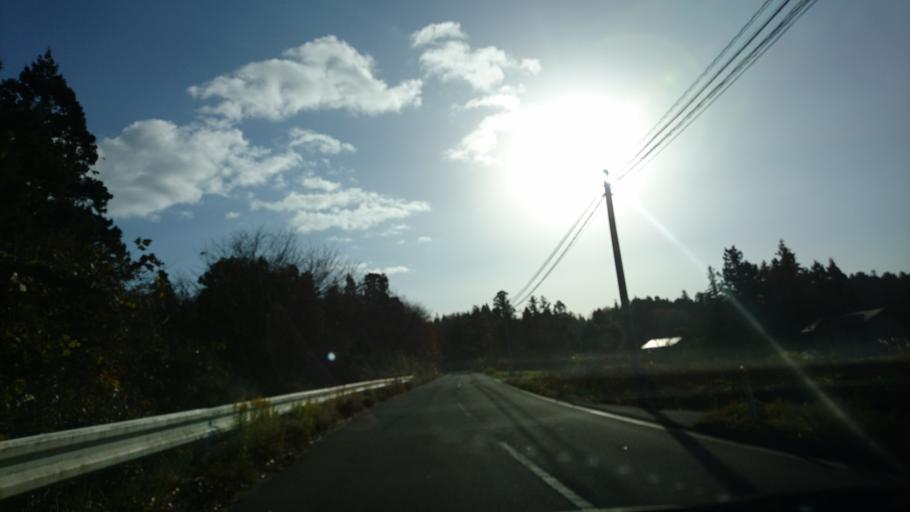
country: JP
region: Iwate
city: Ichinoseki
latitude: 38.8882
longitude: 141.2875
